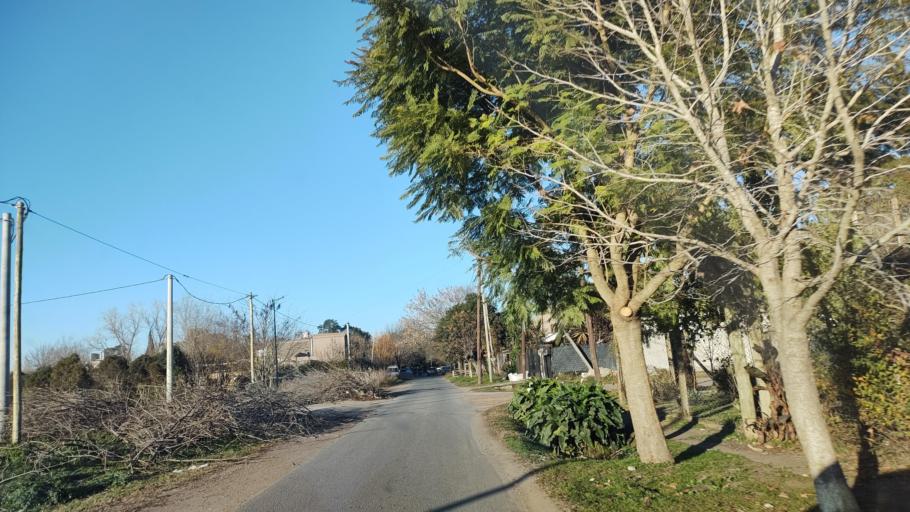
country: AR
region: Buenos Aires
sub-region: Partido de La Plata
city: La Plata
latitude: -34.8807
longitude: -58.0768
